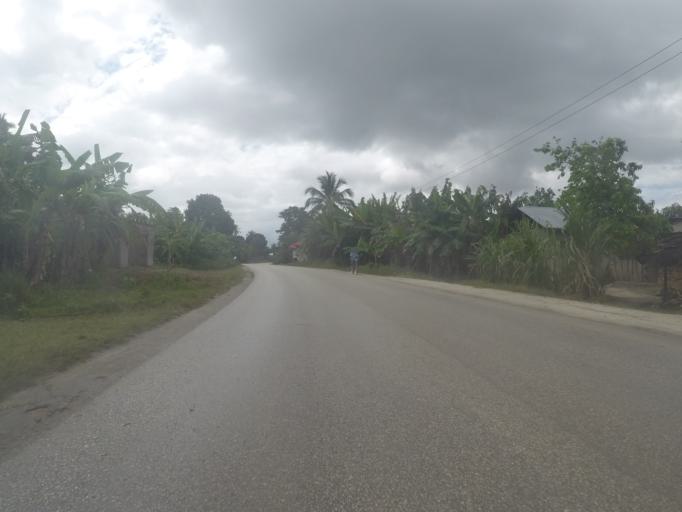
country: TZ
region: Zanzibar North
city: Gamba
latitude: -5.9698
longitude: 39.2527
